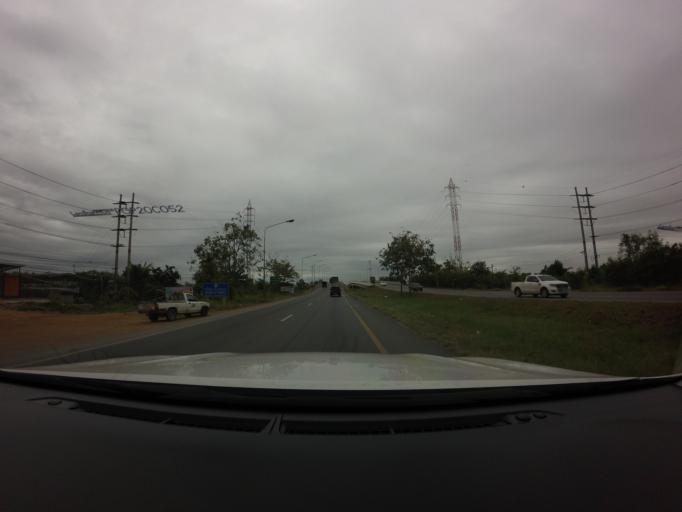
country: TH
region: Chachoengsao
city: Chachoengsao
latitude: 13.6593
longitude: 101.0611
